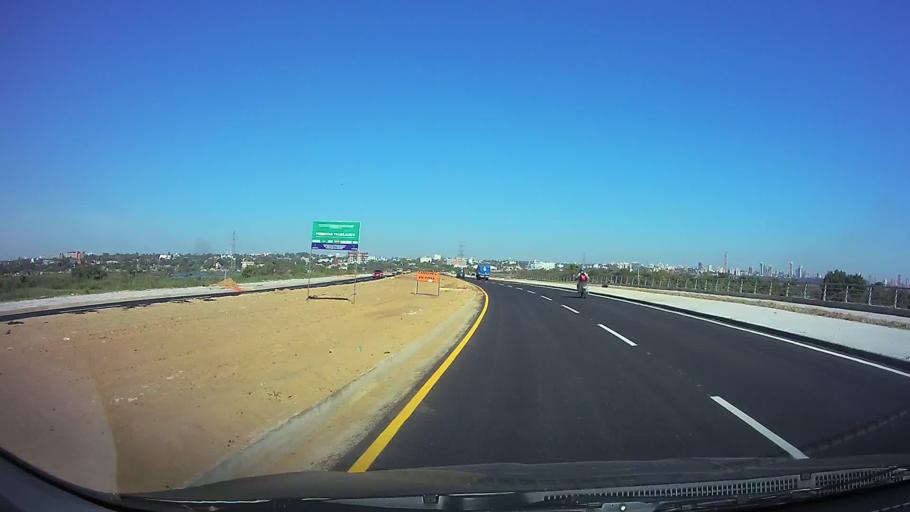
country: PY
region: Asuncion
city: Asuncion
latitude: -25.2573
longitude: -57.6081
